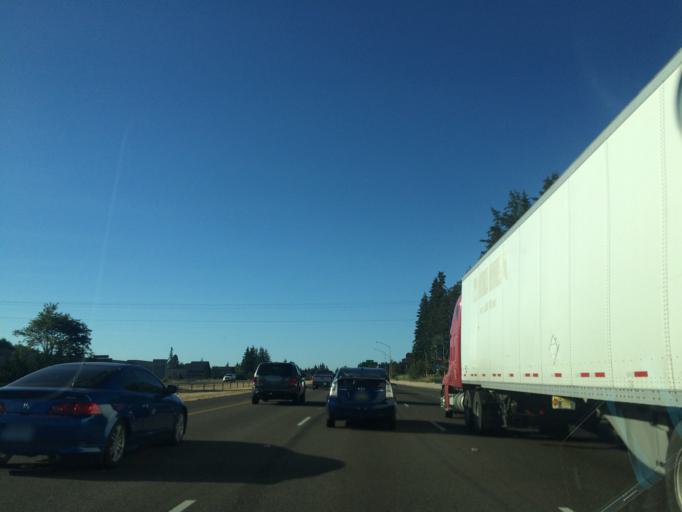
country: US
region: Oregon
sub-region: Clackamas County
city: Wilsonville
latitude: 45.2971
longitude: -122.7691
